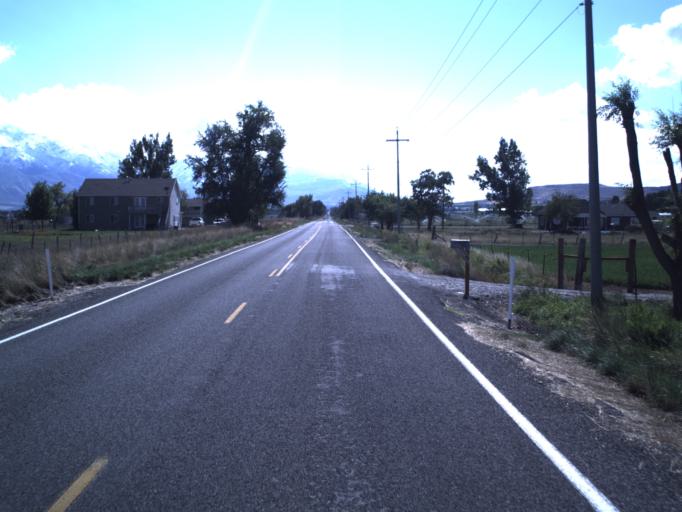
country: US
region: Utah
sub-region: Utah County
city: West Mountain
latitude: 40.0795
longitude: -111.7879
